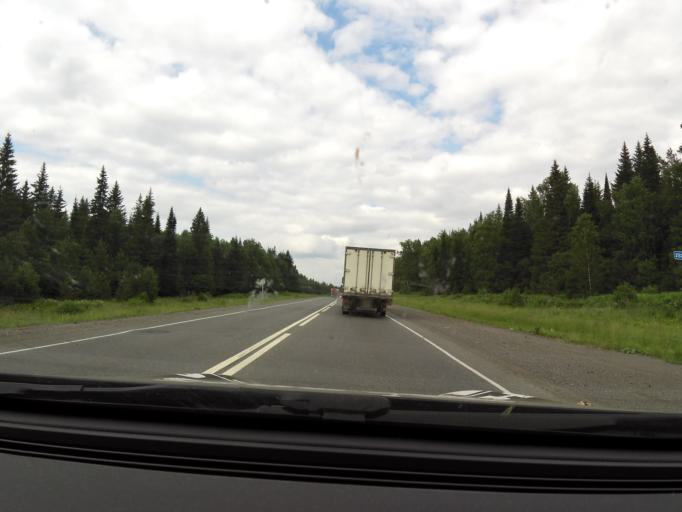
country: RU
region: Sverdlovsk
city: Druzhinino
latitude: 56.8141
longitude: 59.5594
